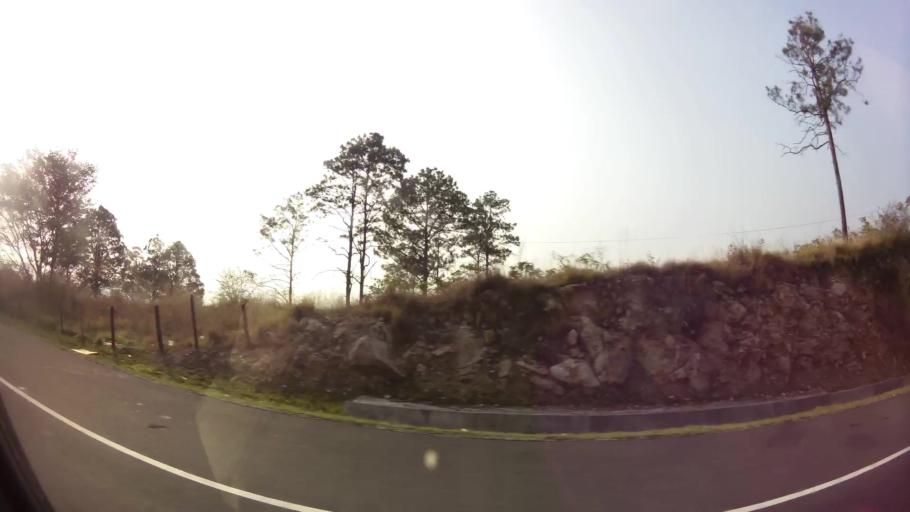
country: HN
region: Francisco Morazan
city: Zambrano
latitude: 14.2399
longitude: -87.3850
